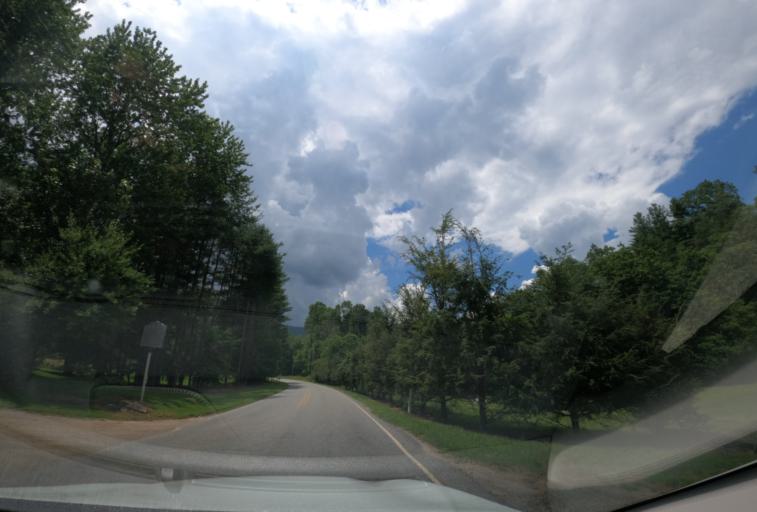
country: US
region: North Carolina
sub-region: Haywood County
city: Waynesville
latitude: 35.4301
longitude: -82.9211
